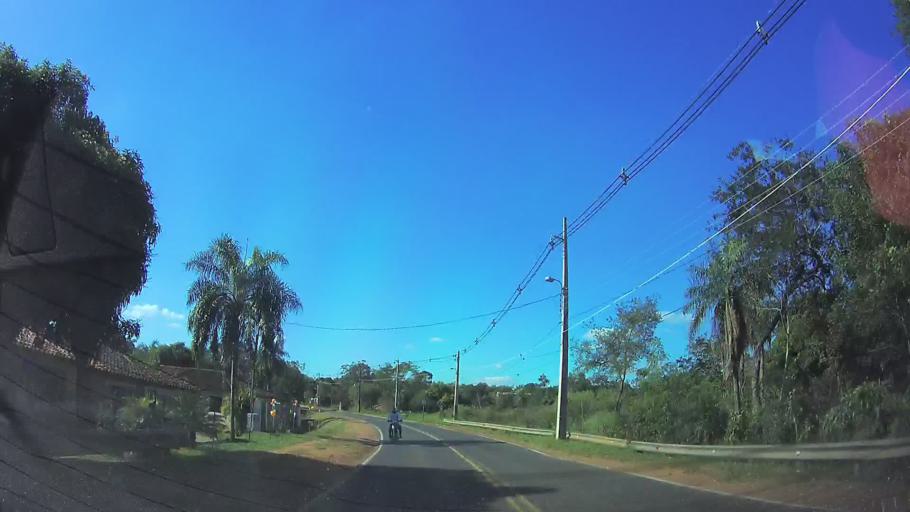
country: PY
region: Central
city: Limpio
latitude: -25.2187
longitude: -57.4755
